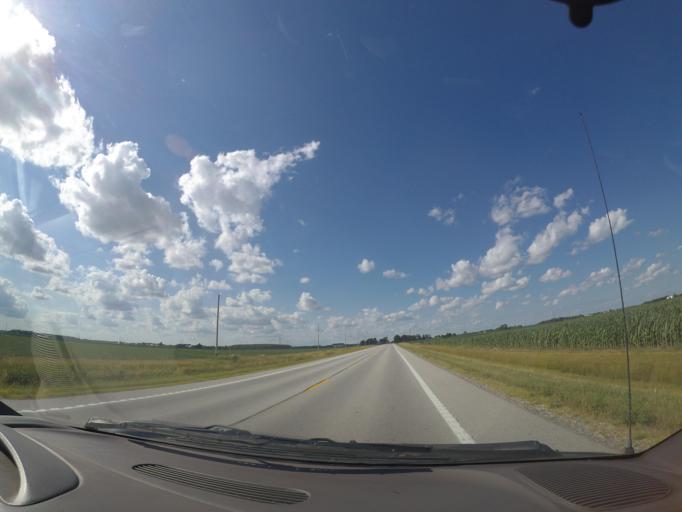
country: US
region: Ohio
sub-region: Wood County
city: Pemberville
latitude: 41.3582
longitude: -83.4169
